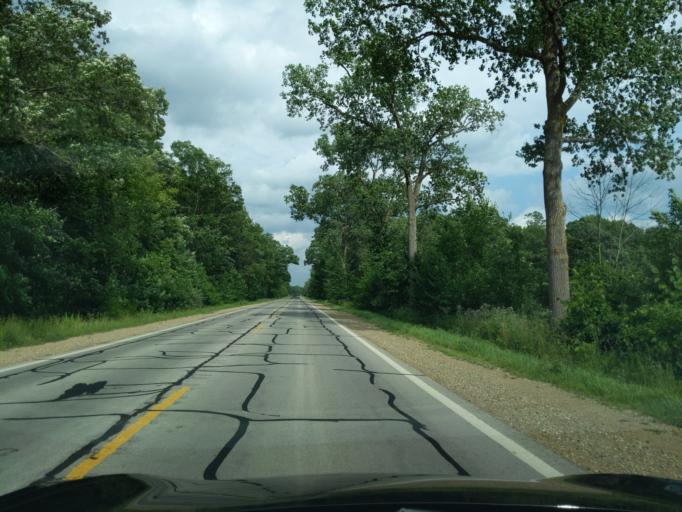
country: US
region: Michigan
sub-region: Eaton County
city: Eaton Rapids
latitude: 42.4149
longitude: -84.6316
